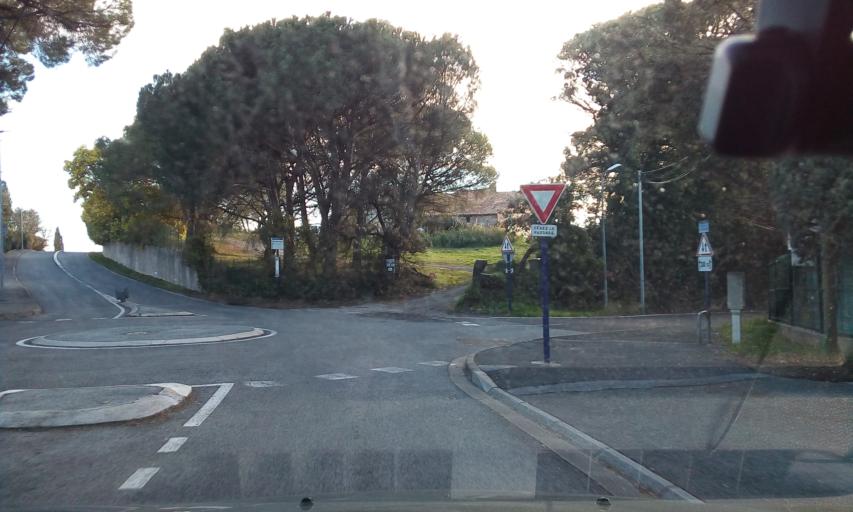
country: FR
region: Provence-Alpes-Cote d'Azur
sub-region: Departement du Var
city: Saint-Raphael
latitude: 43.4413
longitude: 6.7670
